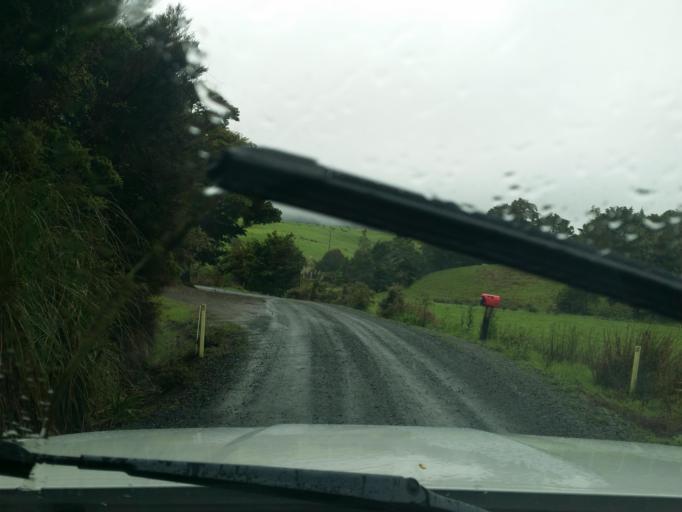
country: NZ
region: Northland
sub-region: Kaipara District
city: Dargaville
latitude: -35.7810
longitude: 173.9522
